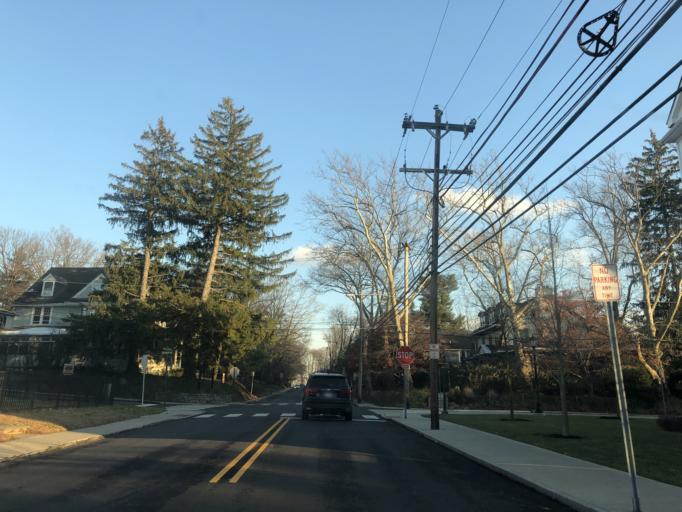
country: US
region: Pennsylvania
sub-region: Montgomery County
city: Bryn Mawr
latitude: 40.0191
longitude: -75.3182
